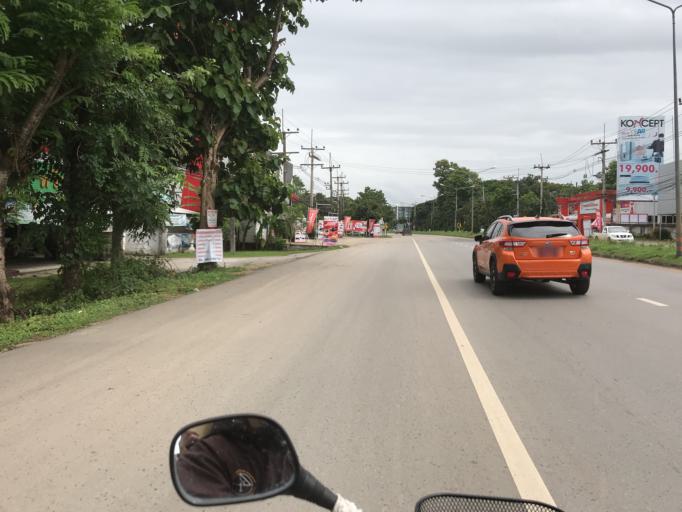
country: TH
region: Chiang Rai
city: Chiang Rai
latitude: 19.9412
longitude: 99.8459
